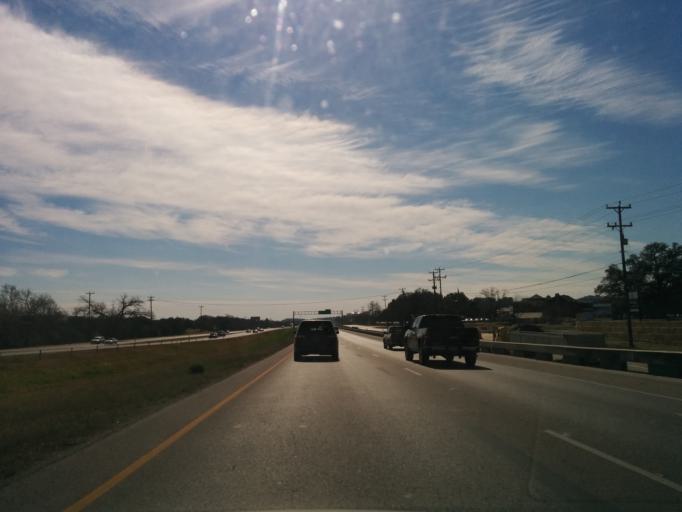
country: US
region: Texas
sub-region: Bexar County
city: Cross Mountain
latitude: 29.6457
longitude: -98.6210
